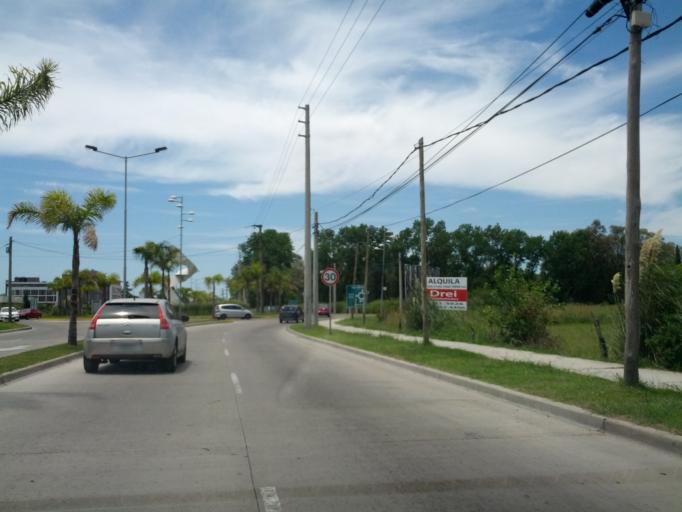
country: AR
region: Buenos Aires
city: Santa Catalina - Dique Lujan
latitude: -34.3945
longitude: -58.6644
